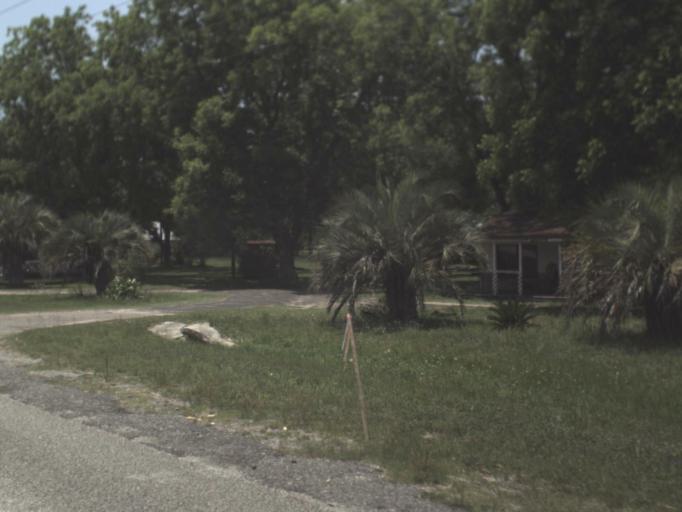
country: US
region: Florida
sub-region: Bradford County
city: Starke
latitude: 29.9929
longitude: -82.0946
